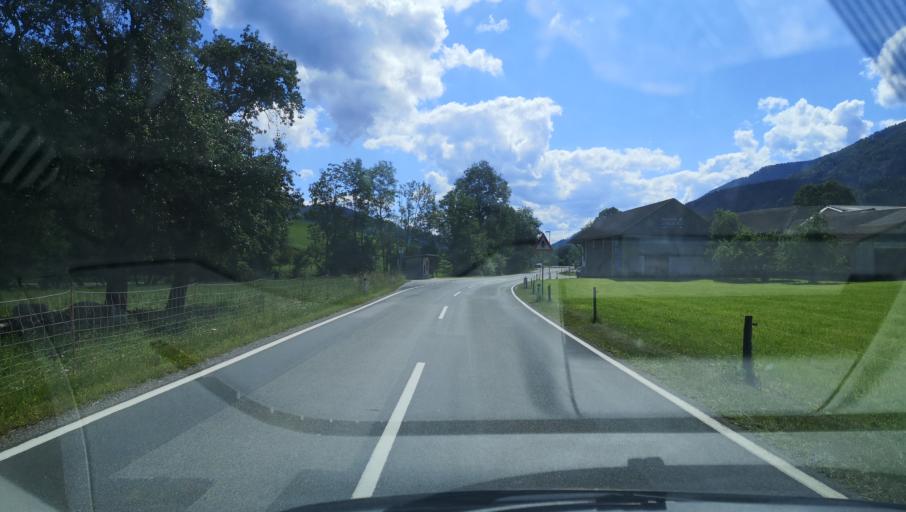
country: AT
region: Lower Austria
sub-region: Politischer Bezirk Scheibbs
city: Gresten
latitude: 47.9577
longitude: 15.0326
